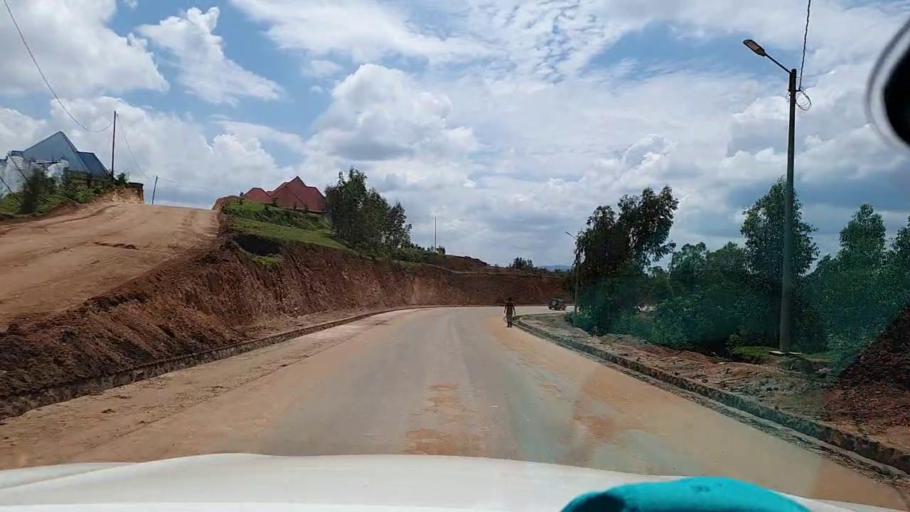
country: RW
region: Southern Province
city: Nzega
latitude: -2.6542
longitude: 29.5593
